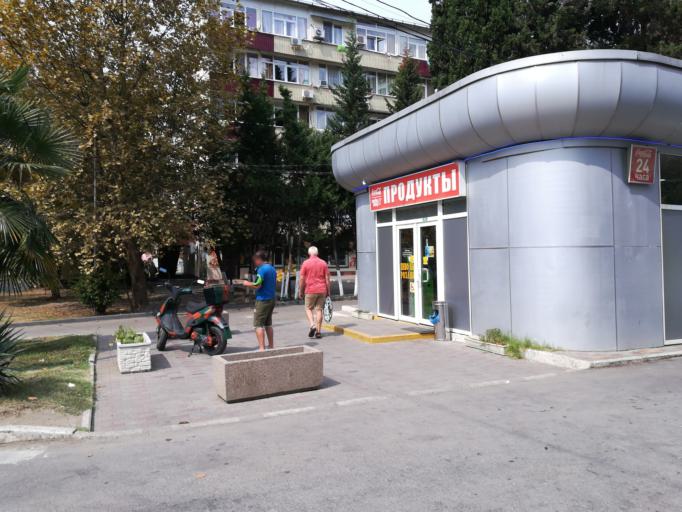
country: RU
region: Krasnodarskiy
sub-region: Sochi City
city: Sochi
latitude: 43.5951
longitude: 39.7353
